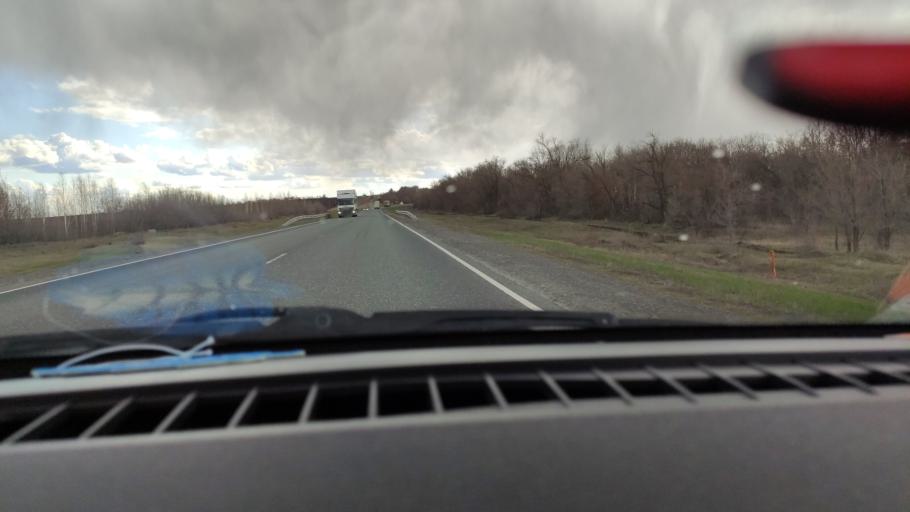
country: RU
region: Saratov
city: Balakovo
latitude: 52.1361
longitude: 47.7954
